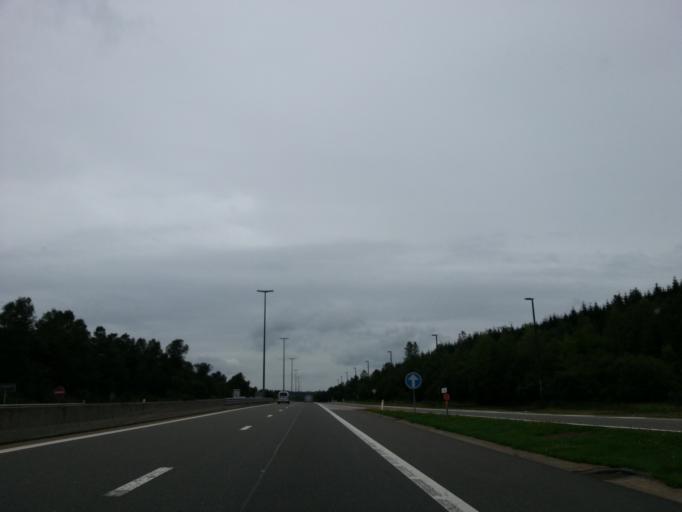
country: BE
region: Wallonia
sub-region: Province de Liege
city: Malmedy
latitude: 50.4615
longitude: 5.9963
